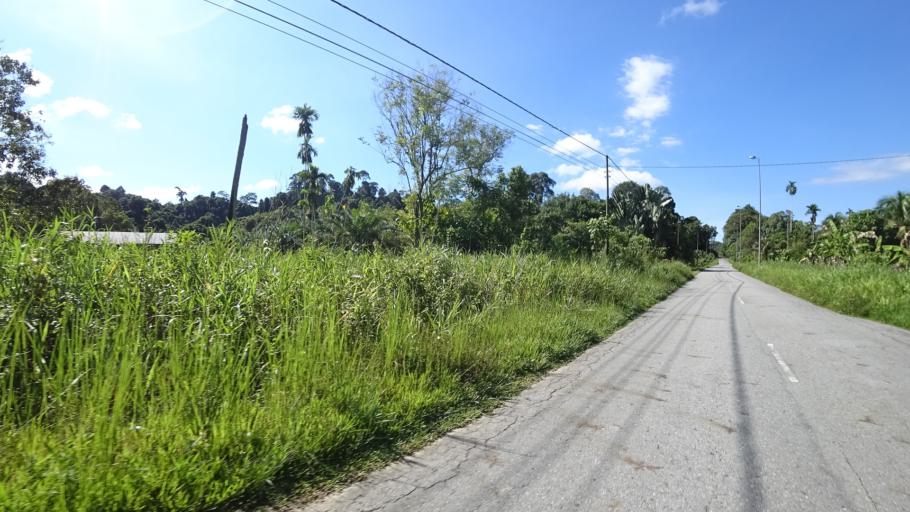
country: BN
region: Tutong
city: Tutong
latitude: 4.7474
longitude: 114.7844
